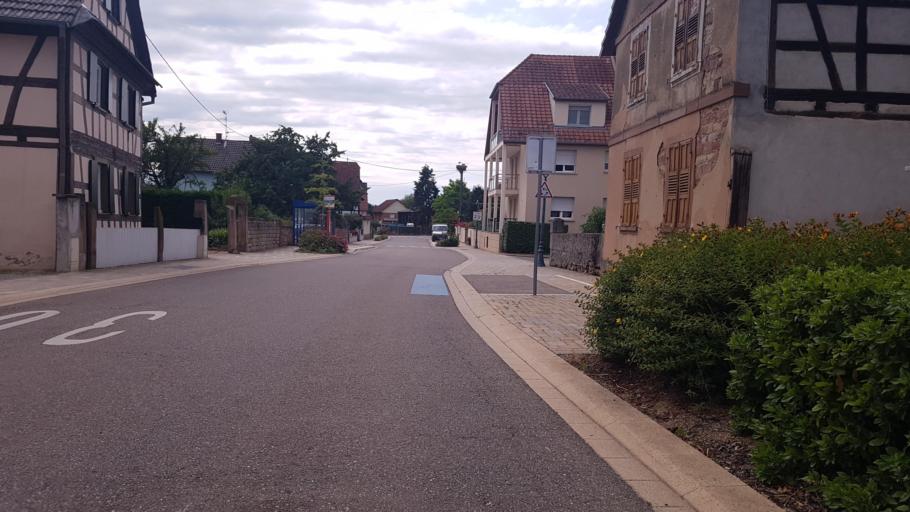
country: FR
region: Alsace
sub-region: Departement du Bas-Rhin
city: Weyersheim
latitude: 48.7189
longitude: 7.7830
